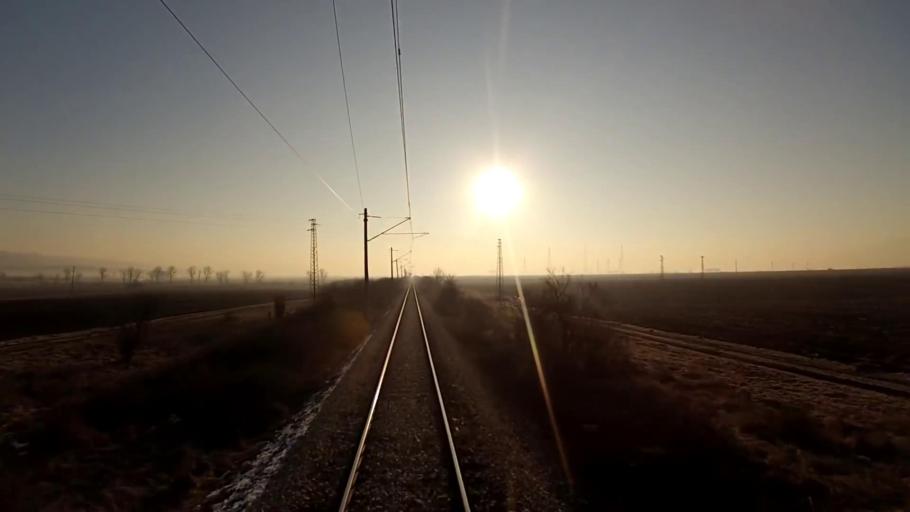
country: BG
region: Sofiya
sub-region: Obshtina Kostinbrod
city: Kostinbrod
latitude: 42.8160
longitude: 23.1831
